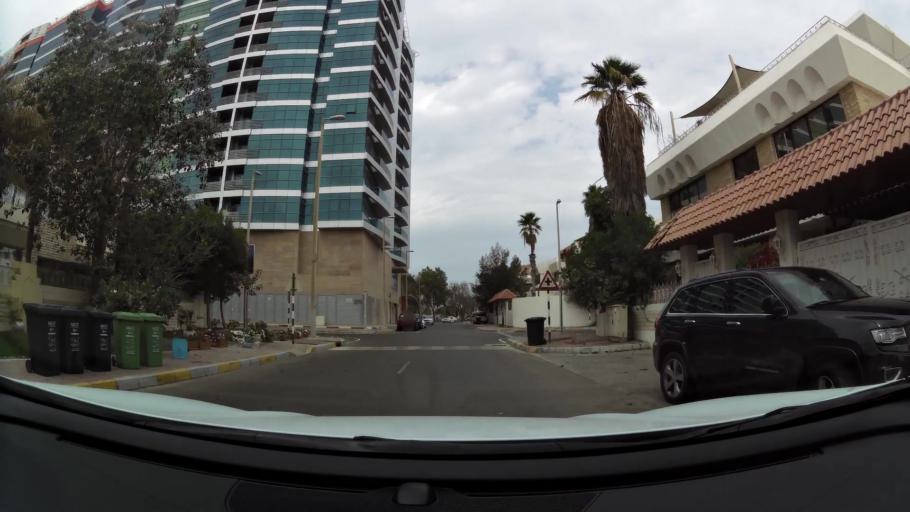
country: AE
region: Abu Dhabi
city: Abu Dhabi
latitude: 24.4673
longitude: 54.3354
